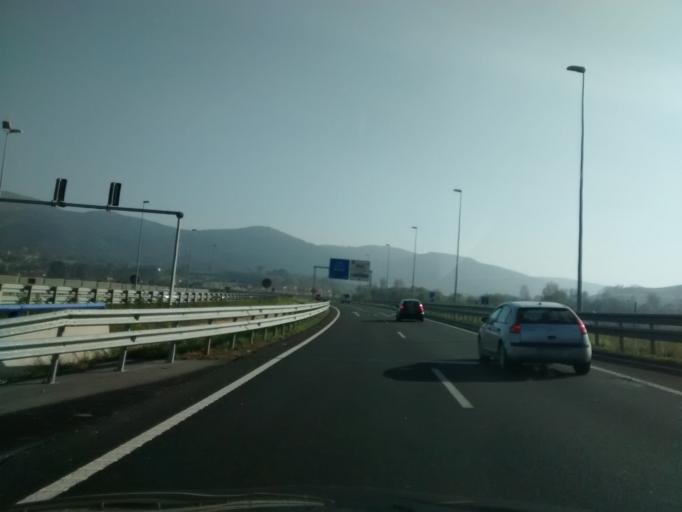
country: ES
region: Cantabria
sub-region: Provincia de Cantabria
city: Camargo
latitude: 43.3886
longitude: -3.8651
